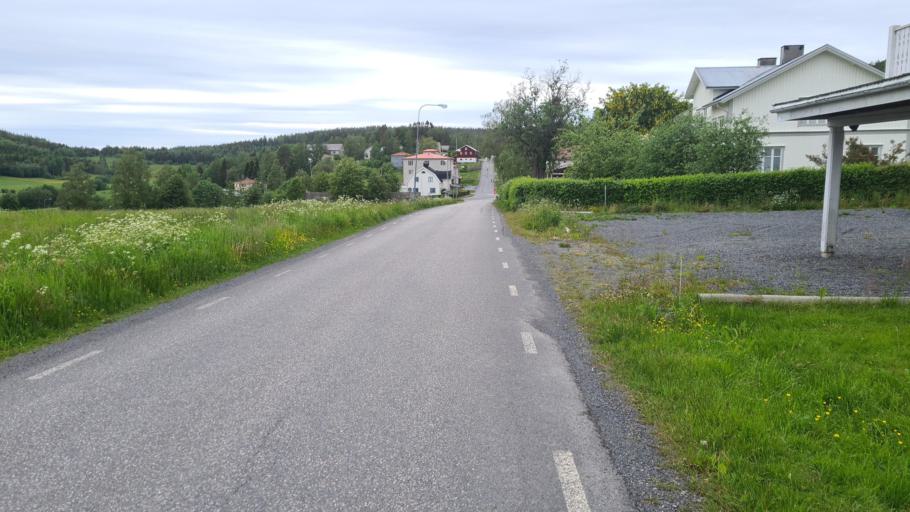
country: SE
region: Vaesternorrland
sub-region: Kramfors Kommun
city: Nordingra
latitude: 62.9844
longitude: 18.4320
